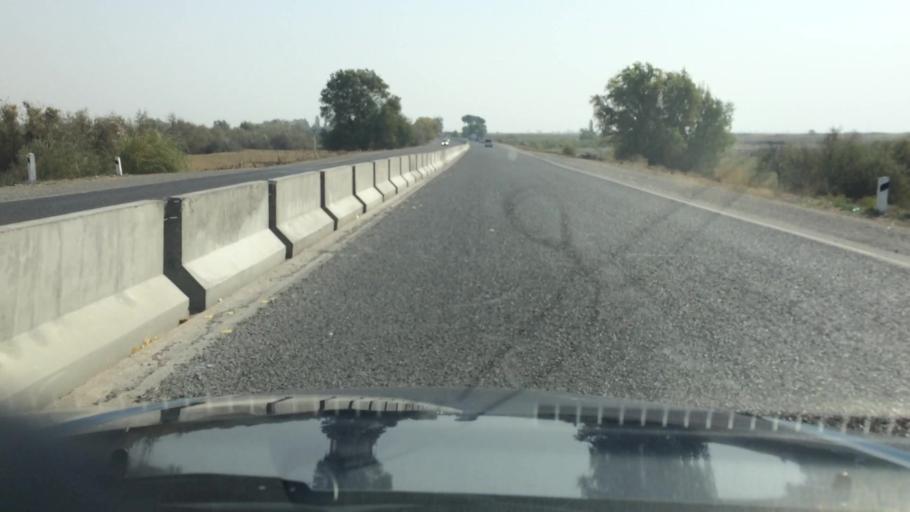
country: KG
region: Chuy
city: Kant
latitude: 42.9609
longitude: 74.9210
